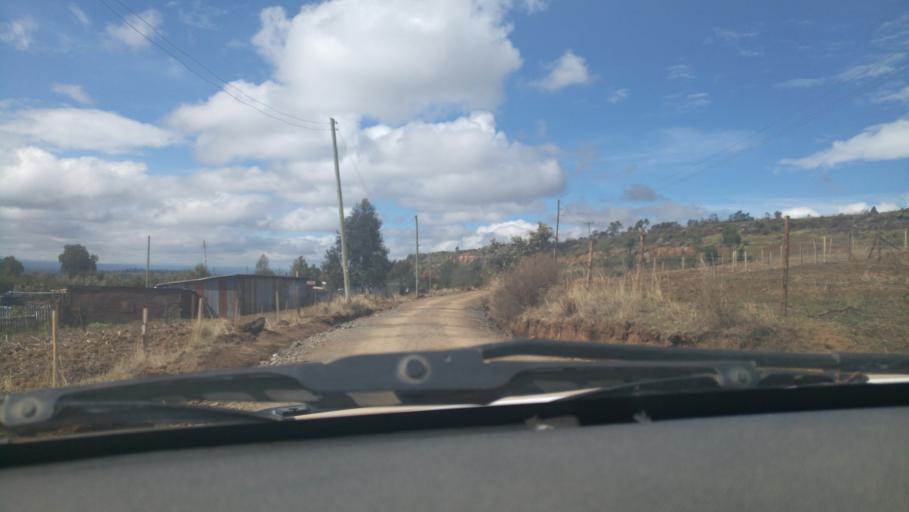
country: KE
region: Nyandarua
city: Ol Kalou
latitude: -0.2778
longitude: 36.3681
